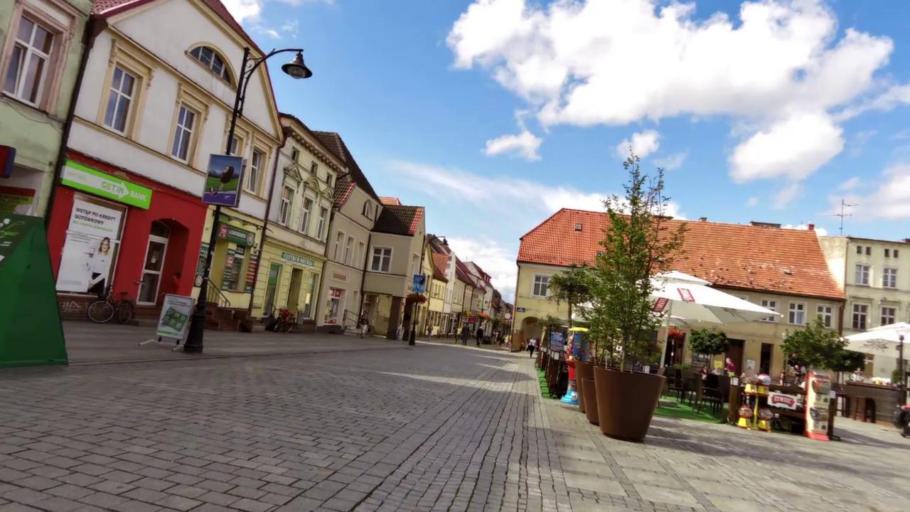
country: PL
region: West Pomeranian Voivodeship
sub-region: Powiat slawienski
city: Darlowo
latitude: 54.4221
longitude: 16.4115
